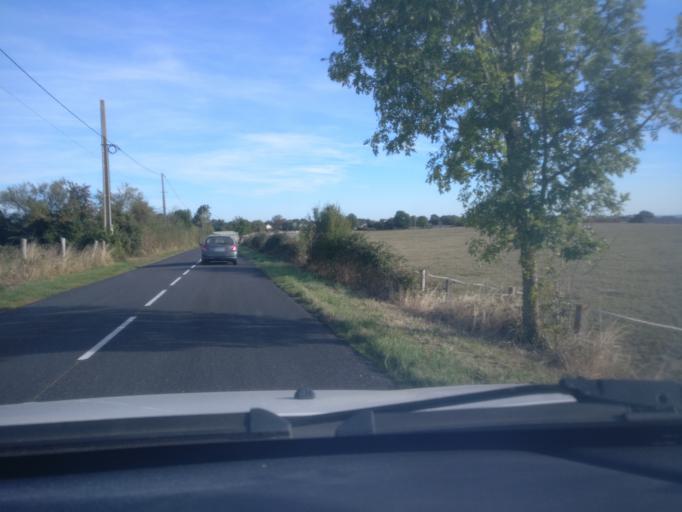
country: FR
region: Lower Normandy
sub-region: Departement de la Manche
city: Sartilly
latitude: 48.7204
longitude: -1.5056
